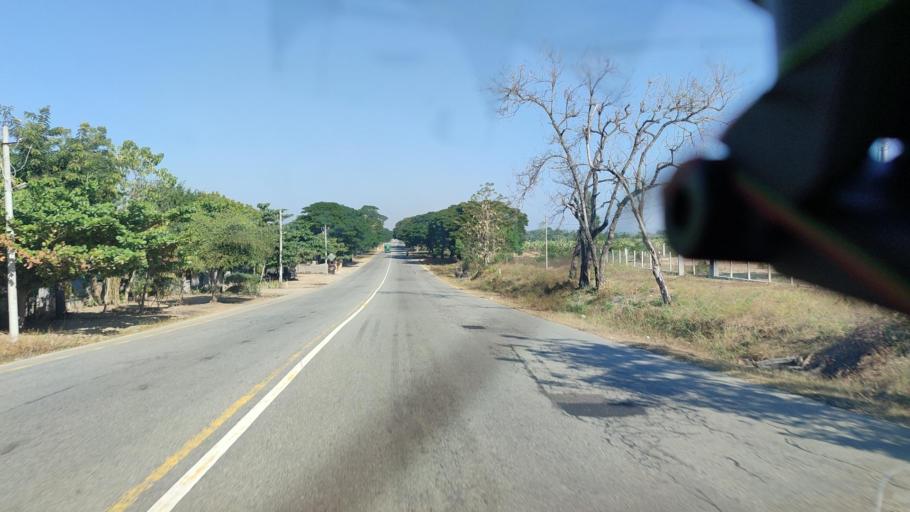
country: MM
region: Mandalay
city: Pyinmana
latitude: 19.9584
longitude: 96.2540
